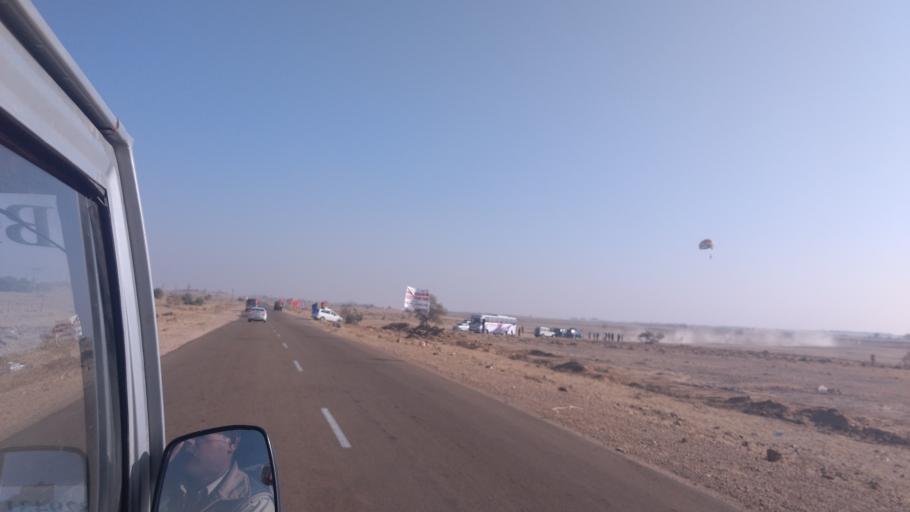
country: IN
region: Rajasthan
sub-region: Jaisalmer
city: Jaisalmer
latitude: 26.8823
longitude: 70.6629
